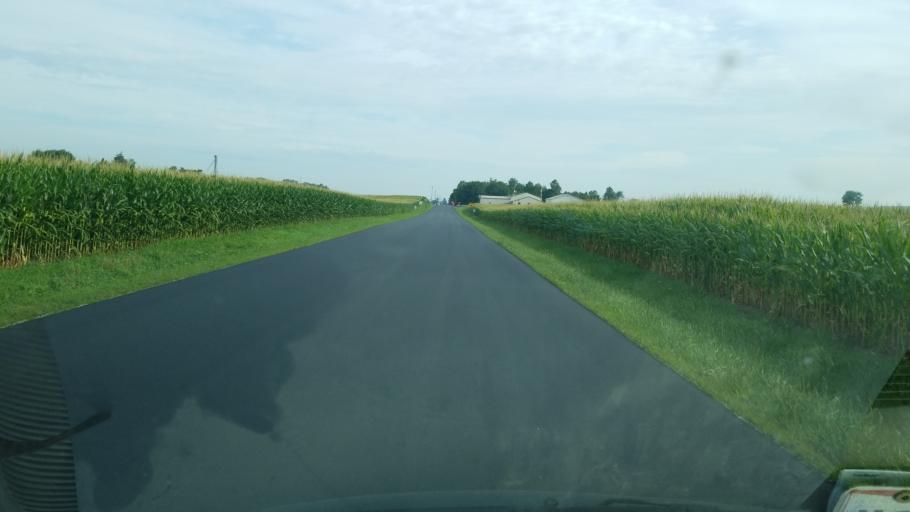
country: US
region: Ohio
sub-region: Crawford County
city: Bucyrus
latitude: 40.8597
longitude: -83.0166
